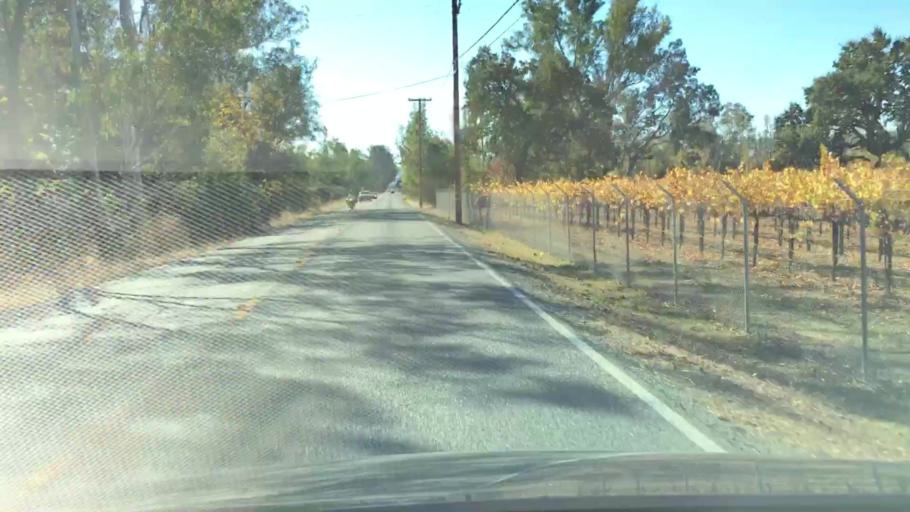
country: US
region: California
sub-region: Sonoma County
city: Sonoma
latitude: 38.2763
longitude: -122.4379
